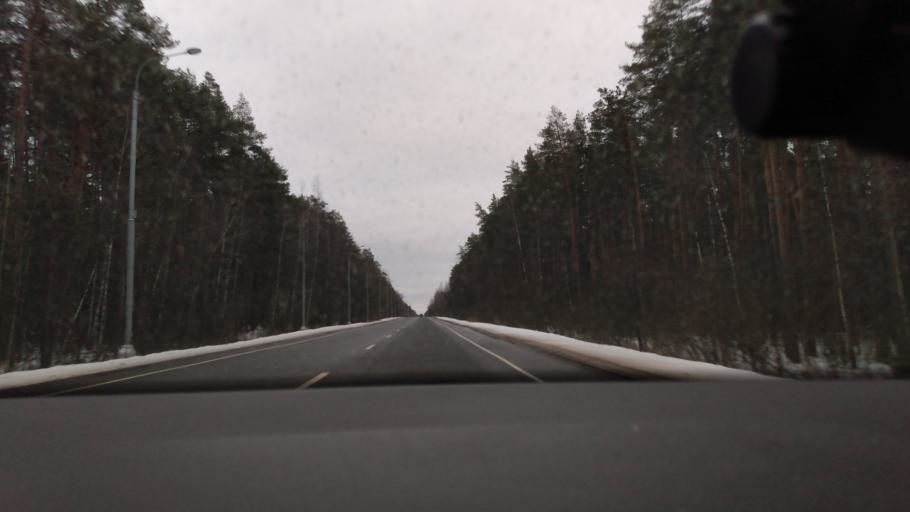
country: RU
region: Moskovskaya
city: Il'inskiy Pogost
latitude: 55.4669
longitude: 38.9698
